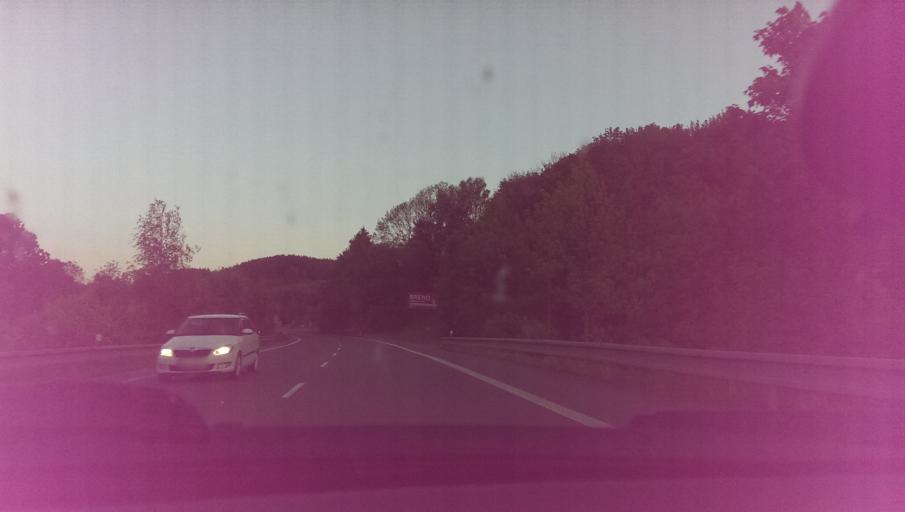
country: CZ
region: Zlin
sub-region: Okres Vsetin
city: Vsetin
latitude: 49.3475
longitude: 17.9705
